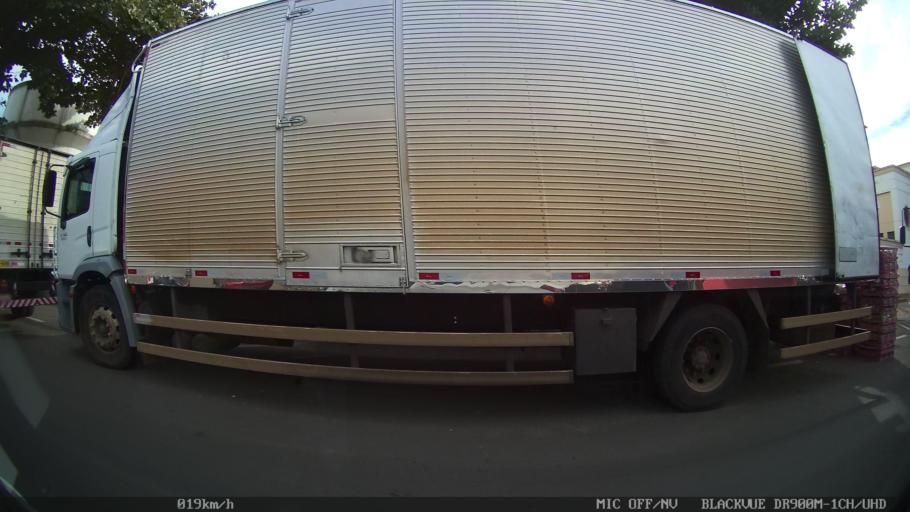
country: BR
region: Sao Paulo
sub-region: Catanduva
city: Catanduva
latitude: -21.1306
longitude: -48.9712
